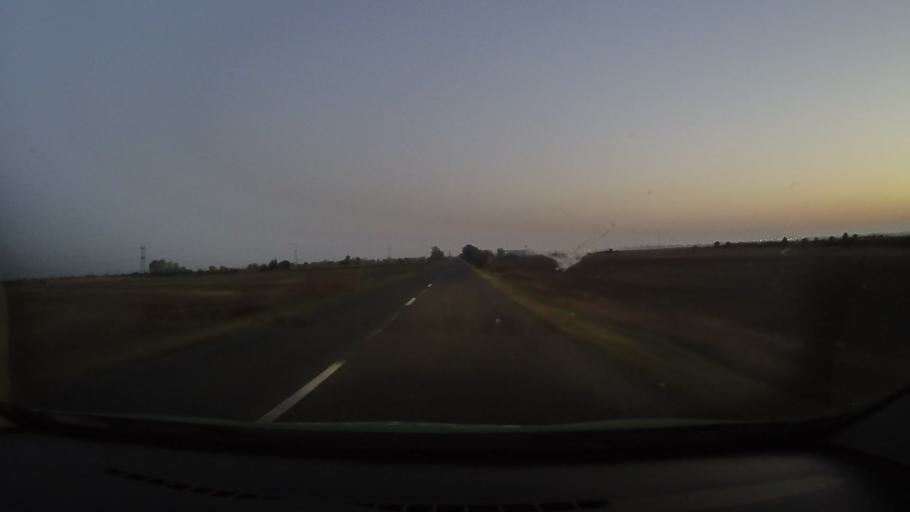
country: RO
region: Arad
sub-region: Comuna Livada
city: Livada
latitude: 46.2020
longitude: 21.3872
